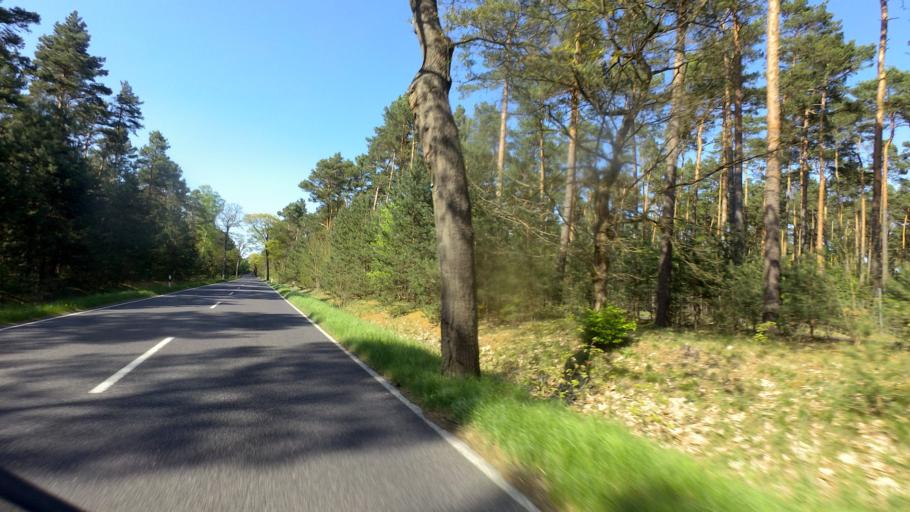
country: DE
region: Brandenburg
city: Halbe
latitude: 52.1272
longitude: 13.7546
